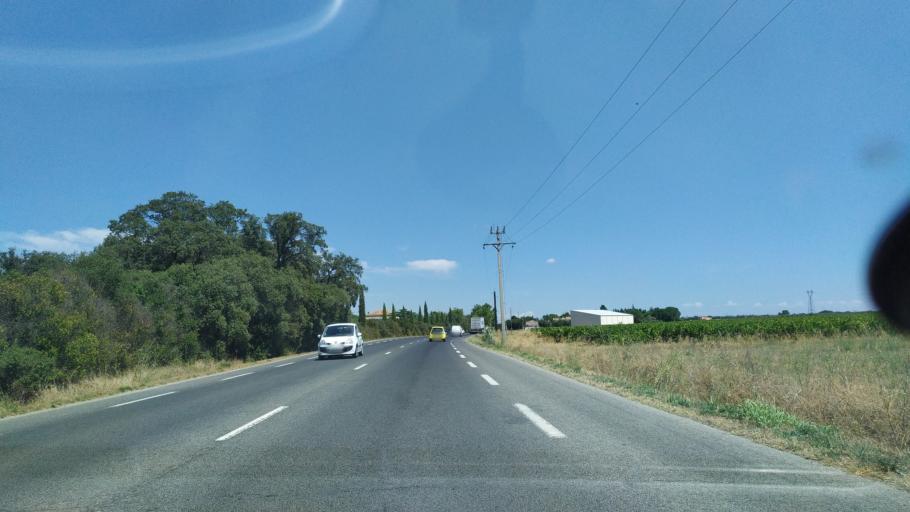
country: FR
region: Languedoc-Roussillon
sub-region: Departement du Gard
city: Aubord
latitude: 43.7645
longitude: 4.3184
